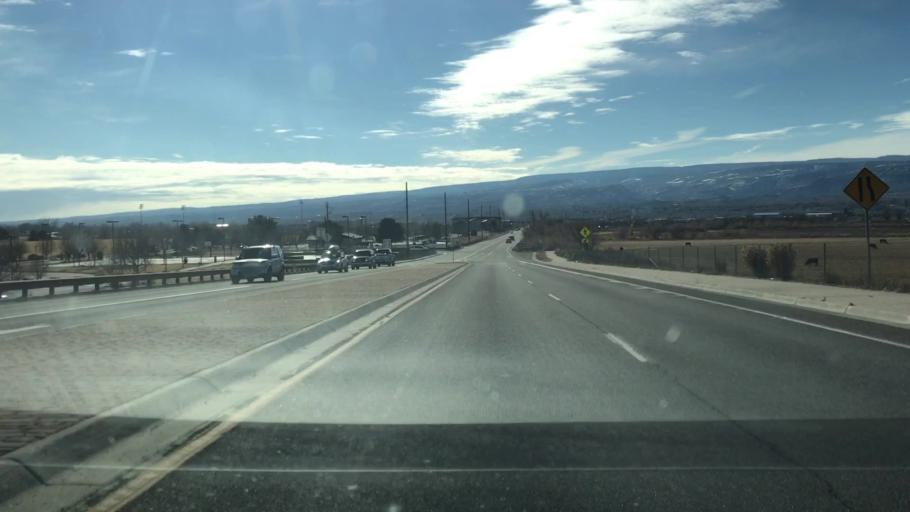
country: US
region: Colorado
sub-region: Mesa County
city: Redlands
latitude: 39.1128
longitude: -108.6083
